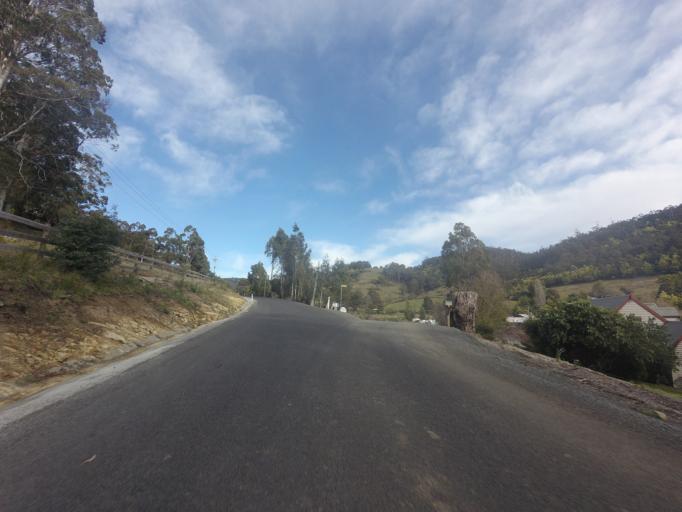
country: AU
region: Tasmania
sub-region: Kingborough
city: Margate
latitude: -42.9913
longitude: 147.1869
